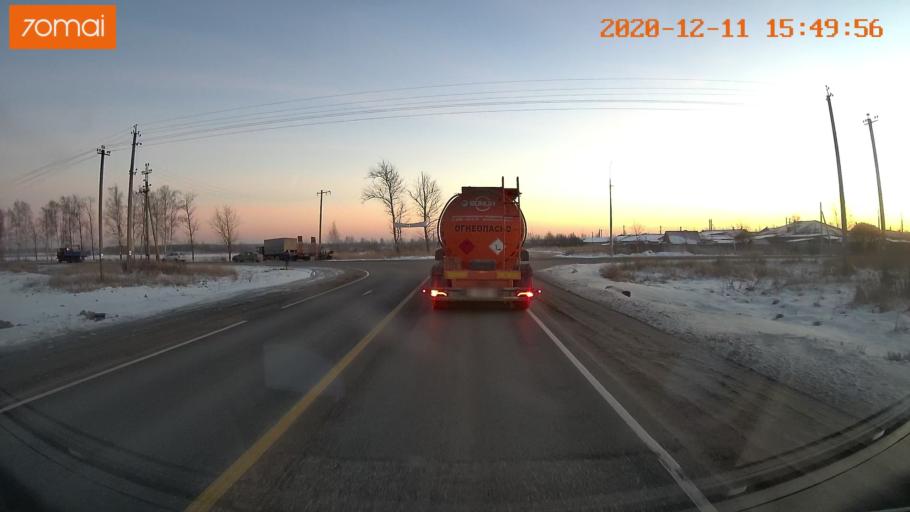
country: RU
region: Ivanovo
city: Novo-Talitsy
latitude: 56.9850
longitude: 40.8786
